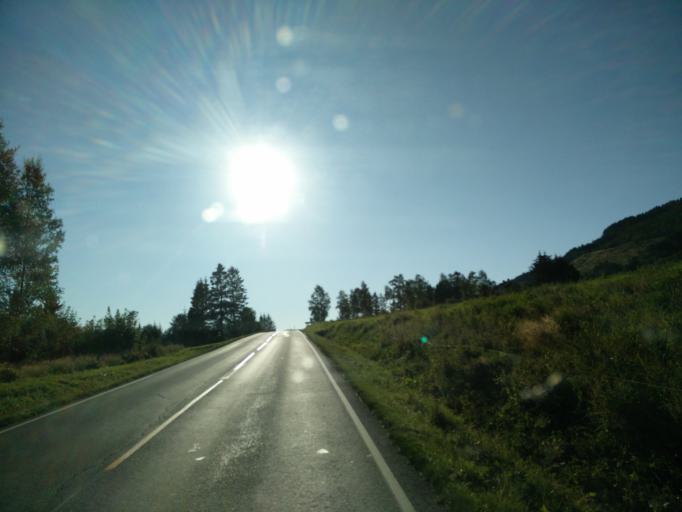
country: NO
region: More og Romsdal
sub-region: Halsa
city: Liaboen
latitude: 63.0722
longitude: 8.2586
